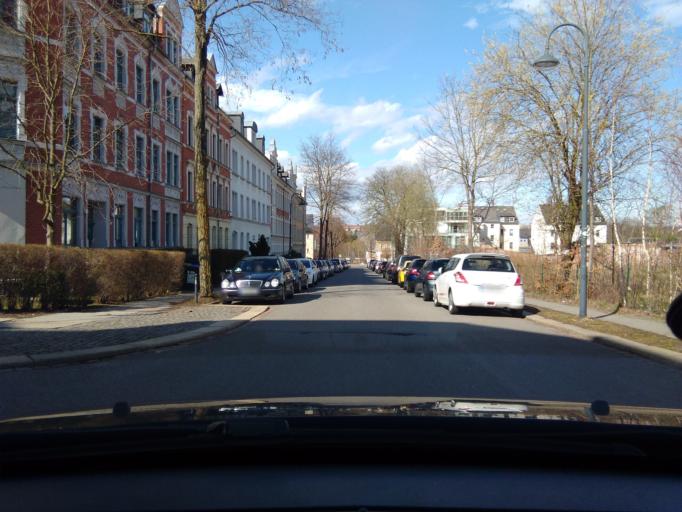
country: DE
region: Saxony
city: Chemnitz
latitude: 50.8342
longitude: 12.8904
